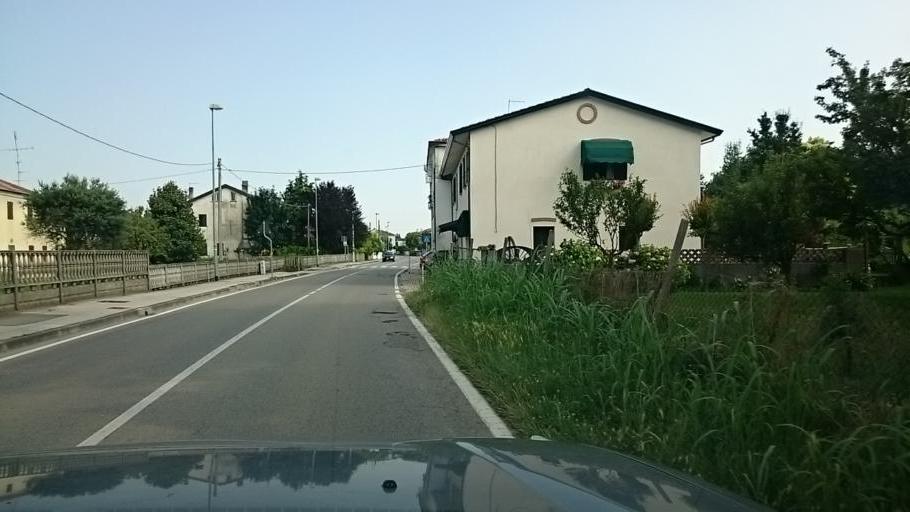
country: IT
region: Veneto
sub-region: Provincia di Padova
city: Saletto
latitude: 45.4798
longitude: 11.8548
